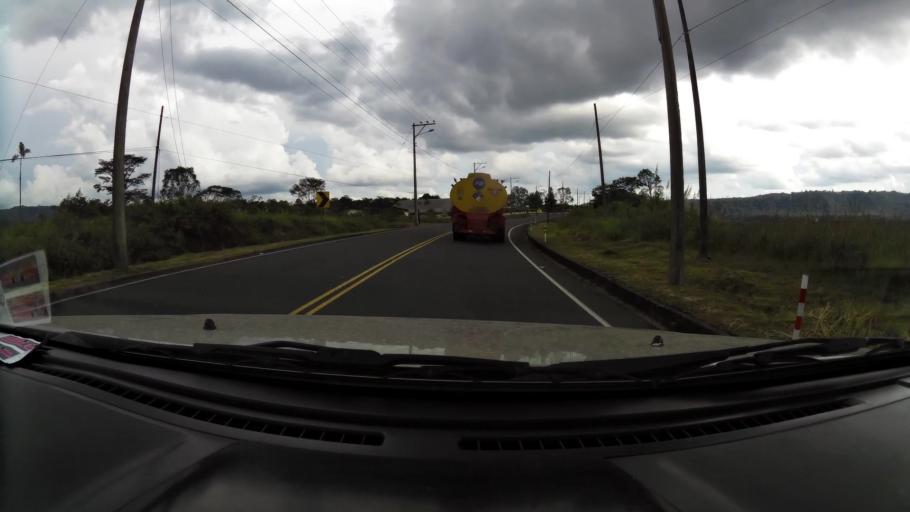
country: EC
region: Pastaza
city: Puyo
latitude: -1.4519
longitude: -78.1235
